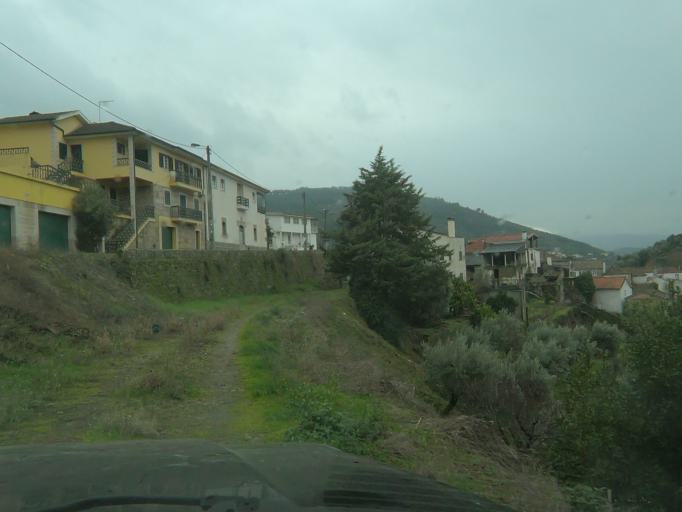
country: PT
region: Vila Real
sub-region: Vila Real
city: Vila Real
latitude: 41.2369
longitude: -7.7396
